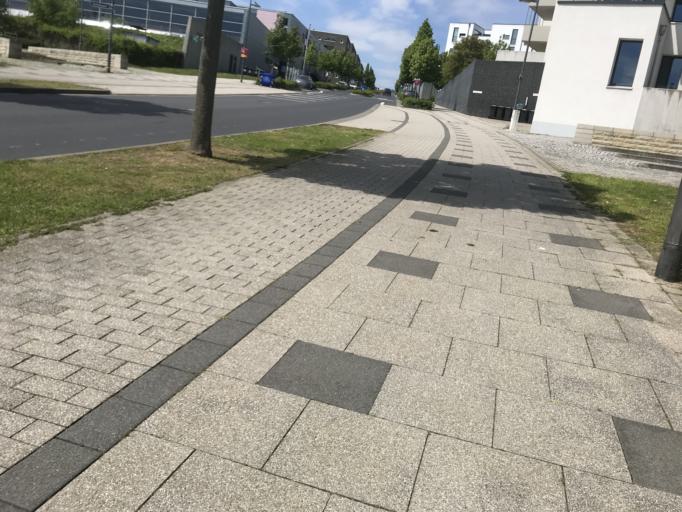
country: DE
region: Hesse
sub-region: Regierungsbezirk Darmstadt
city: Bad Homburg vor der Hoehe
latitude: 50.1778
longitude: 8.6399
